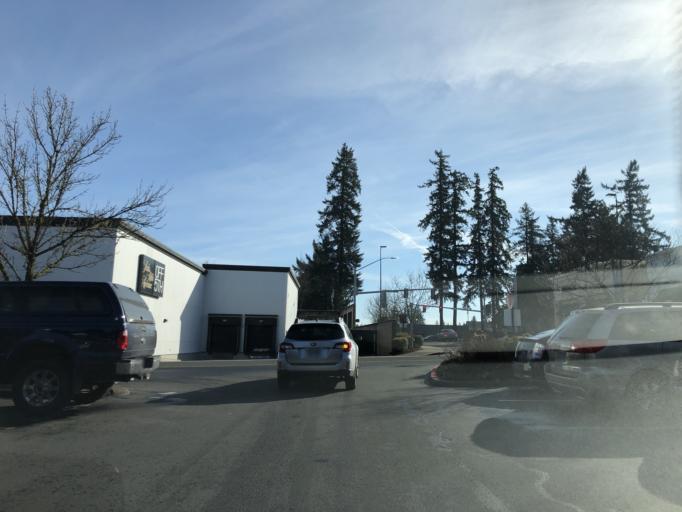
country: US
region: Oregon
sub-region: Washington County
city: Durham
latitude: 45.3949
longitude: -122.7537
